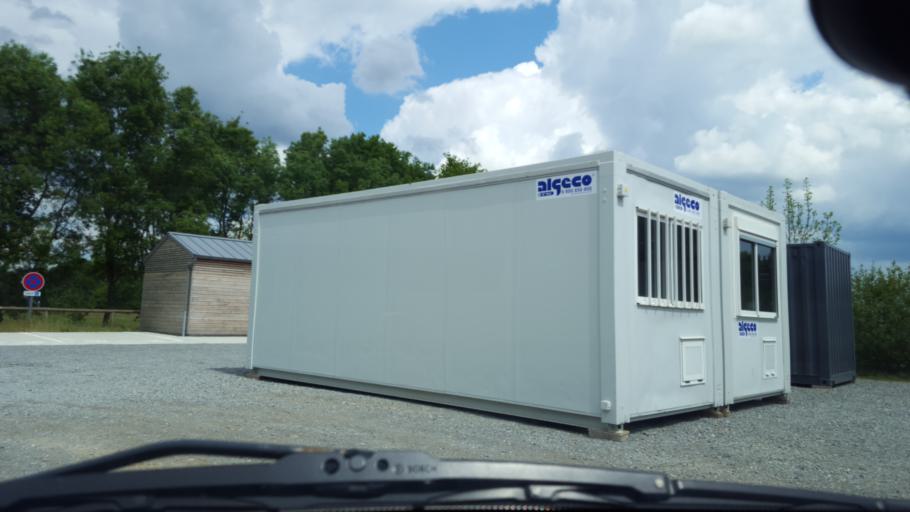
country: FR
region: Pays de la Loire
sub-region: Departement de la Loire-Atlantique
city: Saint-Philbert-de-Grand-Lieu
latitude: 47.0413
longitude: -1.6389
